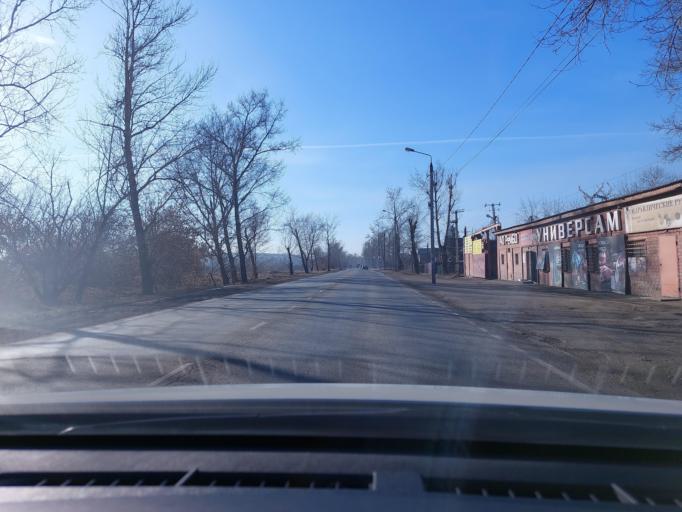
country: RU
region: Irkutsk
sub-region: Irkutskiy Rayon
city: Irkutsk
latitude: 52.3057
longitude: 104.2542
